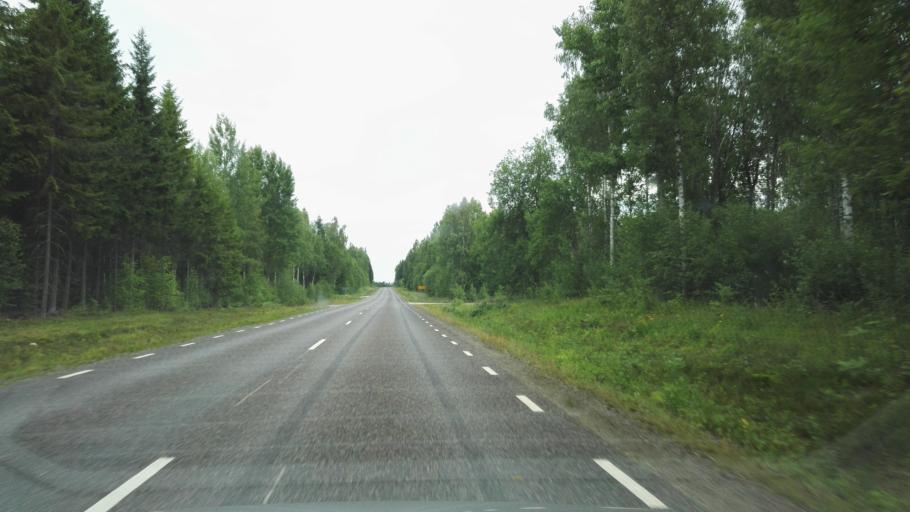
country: SE
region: Kronoberg
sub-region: Vaxjo Kommun
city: Braas
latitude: 57.0886
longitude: 14.9984
